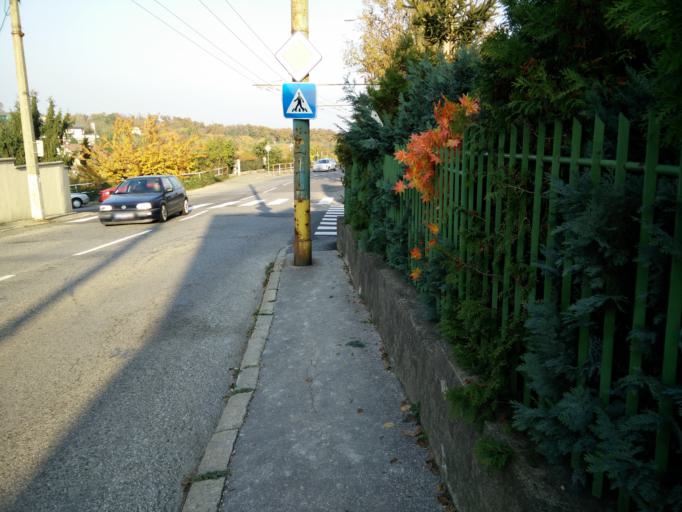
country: SK
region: Bratislavsky
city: Bratislava
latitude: 48.1694
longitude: 17.1071
